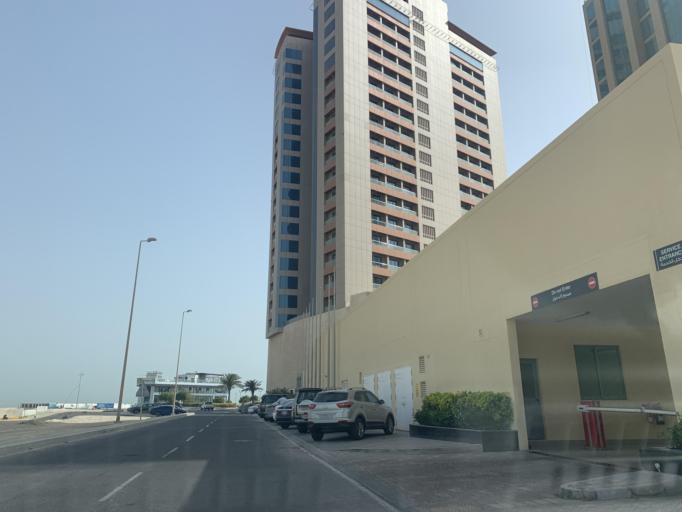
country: BH
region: Manama
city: Jidd Hafs
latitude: 26.2416
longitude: 50.5572
